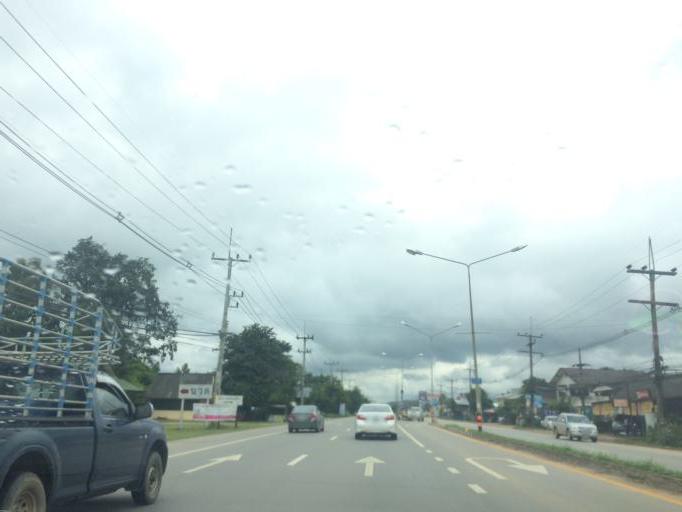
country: TH
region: Chiang Rai
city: Chiang Rai
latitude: 20.0161
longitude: 99.8697
